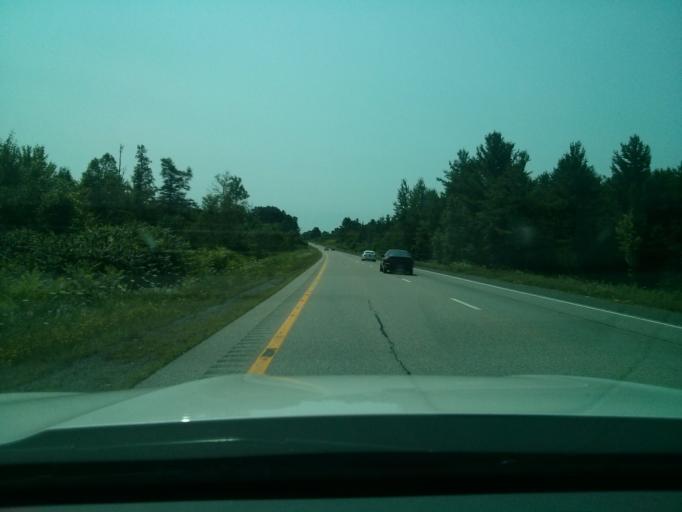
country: CA
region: Ontario
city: Prescott
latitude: 44.9032
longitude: -75.5750
